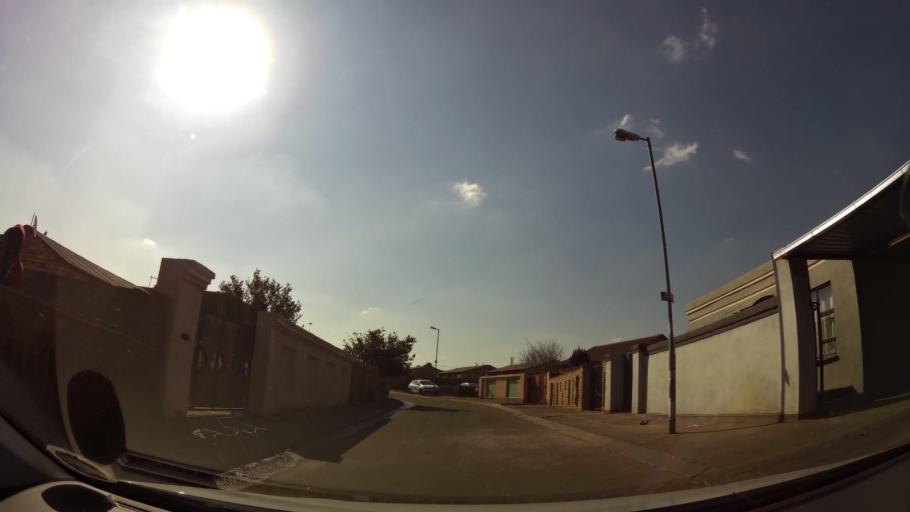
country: ZA
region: Gauteng
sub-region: City of Johannesburg Metropolitan Municipality
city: Soweto
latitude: -26.2843
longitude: 27.8582
